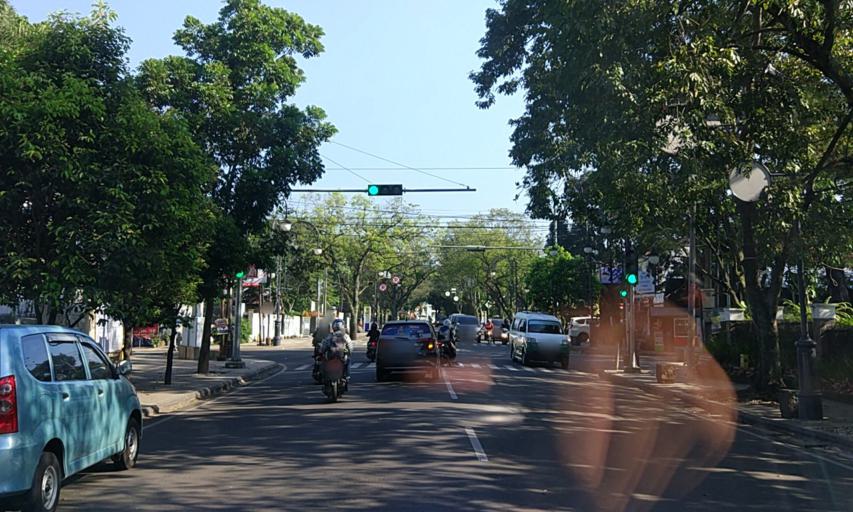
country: ID
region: West Java
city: Bandung
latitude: -6.9079
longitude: 107.6235
